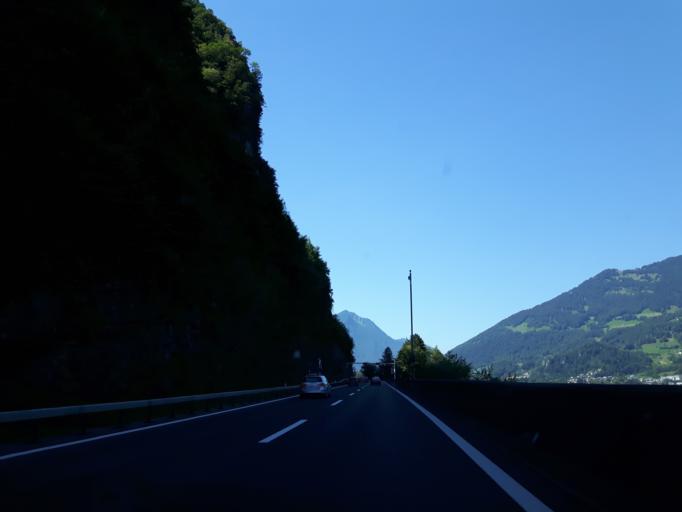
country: CH
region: Saint Gallen
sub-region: Wahlkreis See-Gaster
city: Amden
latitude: 47.1258
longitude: 9.1359
